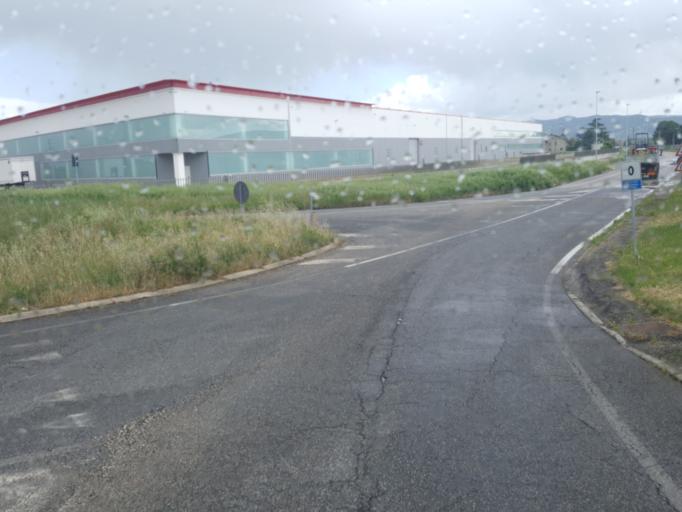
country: IT
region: Umbria
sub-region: Provincia di Perugia
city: Ospedalicchio
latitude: 43.0766
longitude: 12.5026
